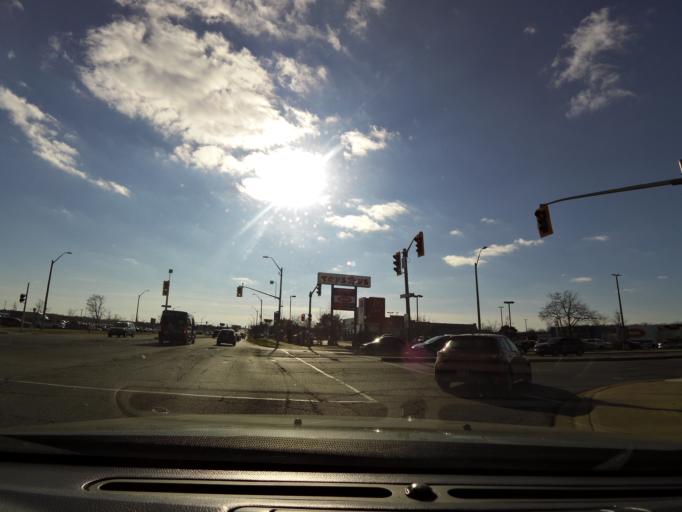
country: CA
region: Ontario
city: Hamilton
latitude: 43.2188
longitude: -79.8640
